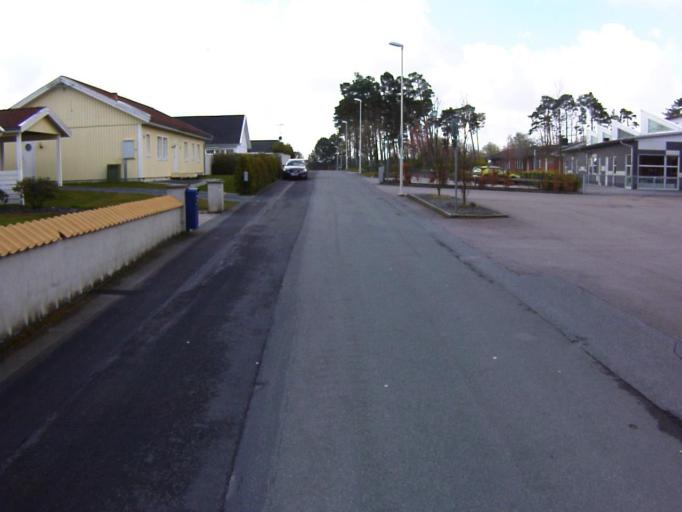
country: SE
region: Skane
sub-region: Kristianstads Kommun
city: Kristianstad
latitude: 56.0120
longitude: 14.0987
